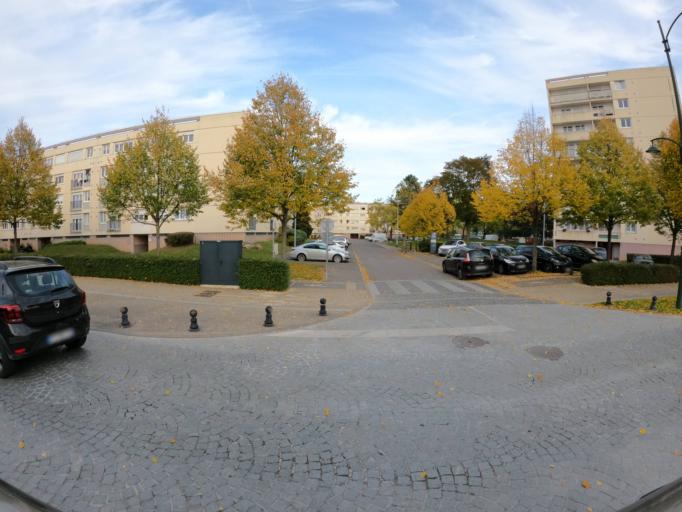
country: FR
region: Ile-de-France
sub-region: Departement de Seine-et-Marne
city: Pontault-Combault
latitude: 48.7975
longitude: 2.6084
